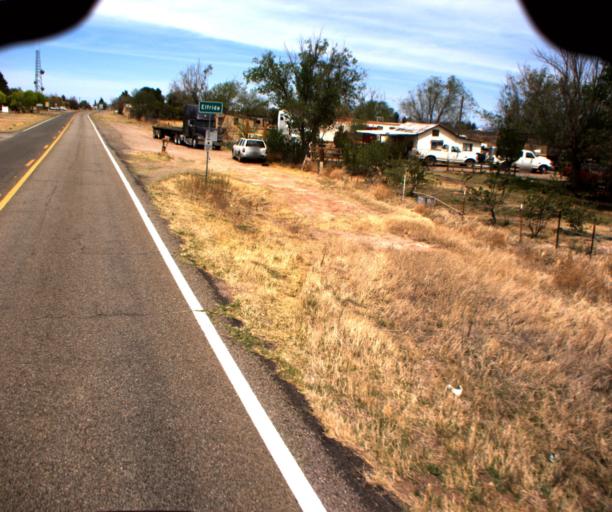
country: US
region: Arizona
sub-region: Cochise County
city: Bisbee
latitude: 31.6765
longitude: -109.6853
